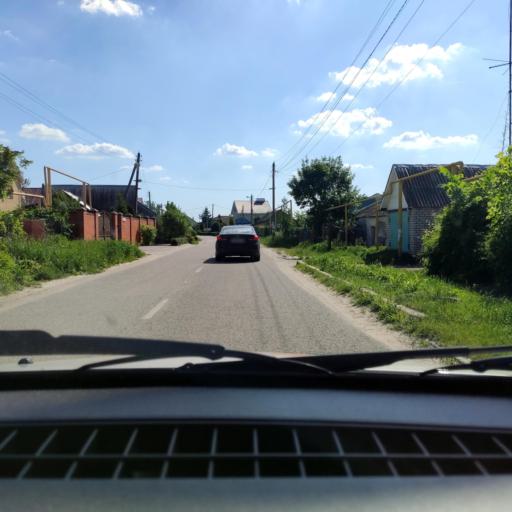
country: RU
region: Voronezj
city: Ramon'
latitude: 51.8181
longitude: 39.2662
